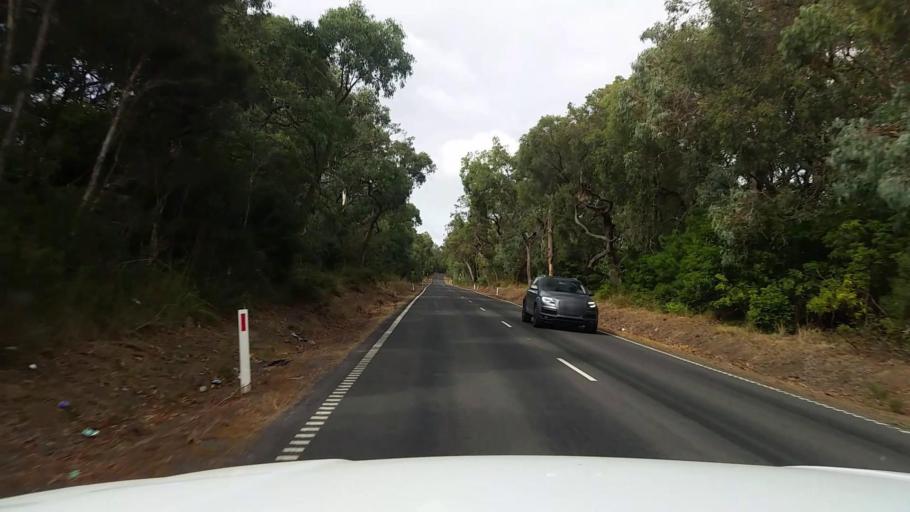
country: AU
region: Victoria
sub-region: Mornington Peninsula
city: Balnarring
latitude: -38.3211
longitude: 145.0906
